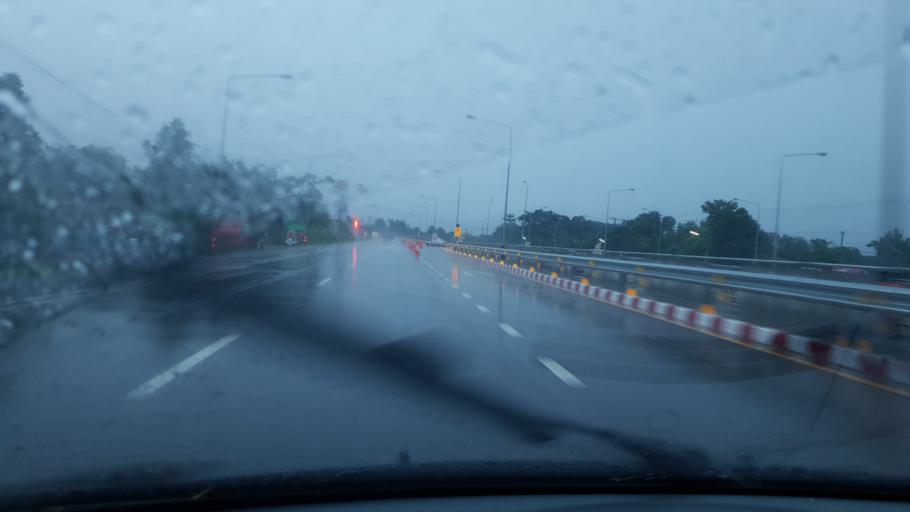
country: TH
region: Chiang Mai
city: San Pa Tong
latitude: 18.6560
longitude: 98.8634
